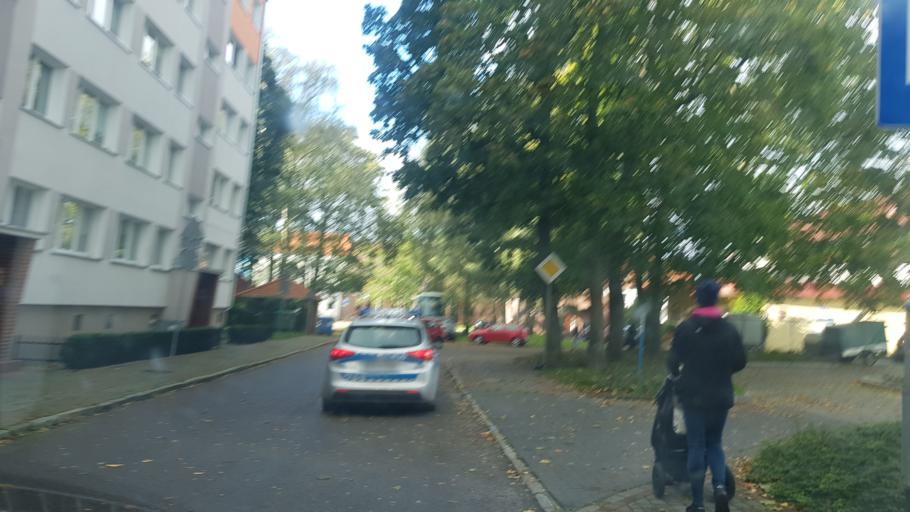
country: PL
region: West Pomeranian Voivodeship
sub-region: Powiat kolobrzeski
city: Kolobrzeg
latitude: 54.1926
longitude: 15.6634
